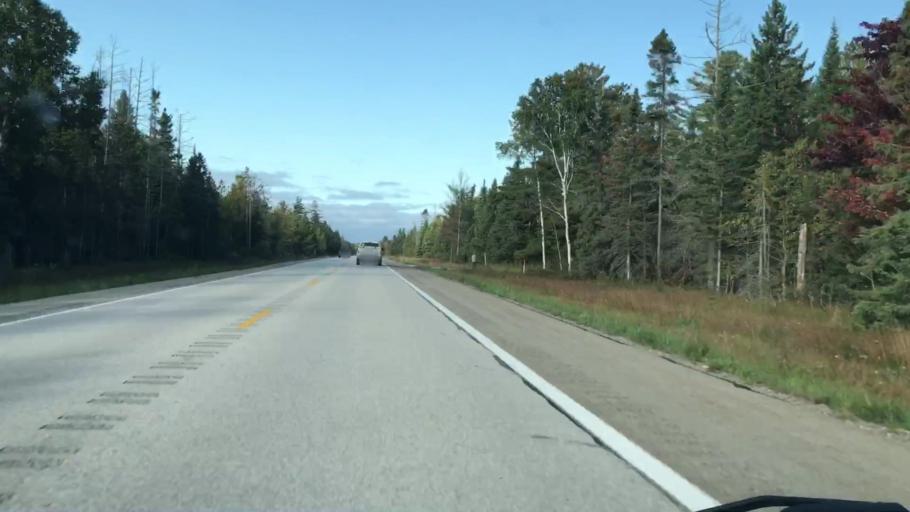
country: US
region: Michigan
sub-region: Luce County
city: Newberry
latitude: 46.3238
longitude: -85.1746
